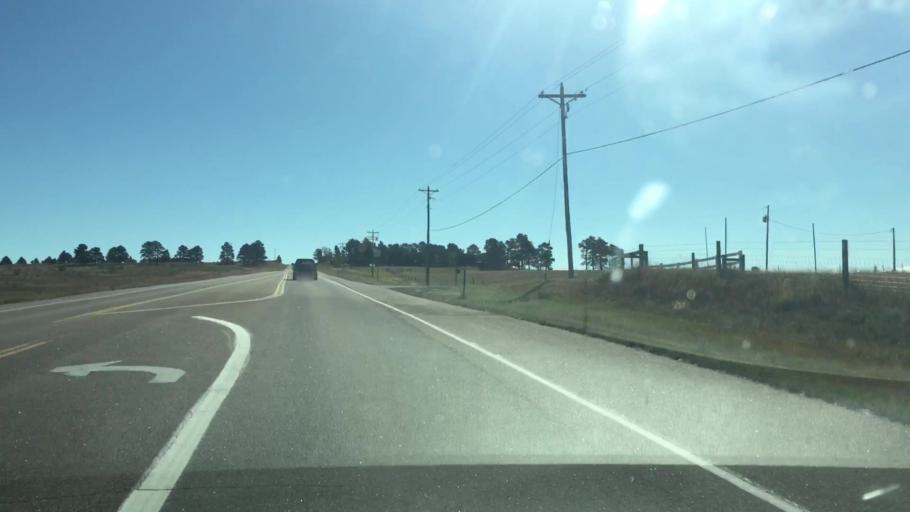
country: US
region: Colorado
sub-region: Elbert County
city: Elizabeth
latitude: 39.3582
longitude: -104.5313
